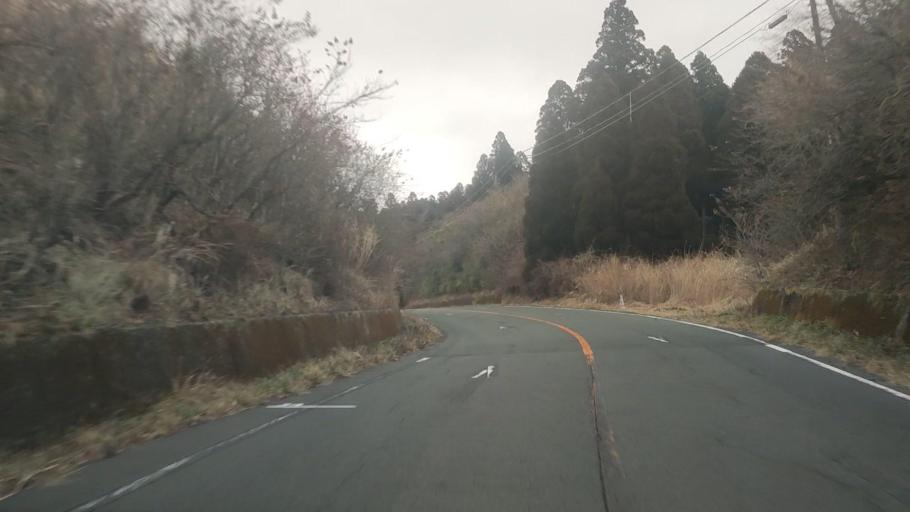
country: JP
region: Kumamoto
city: Aso
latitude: 32.8828
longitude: 131.1708
